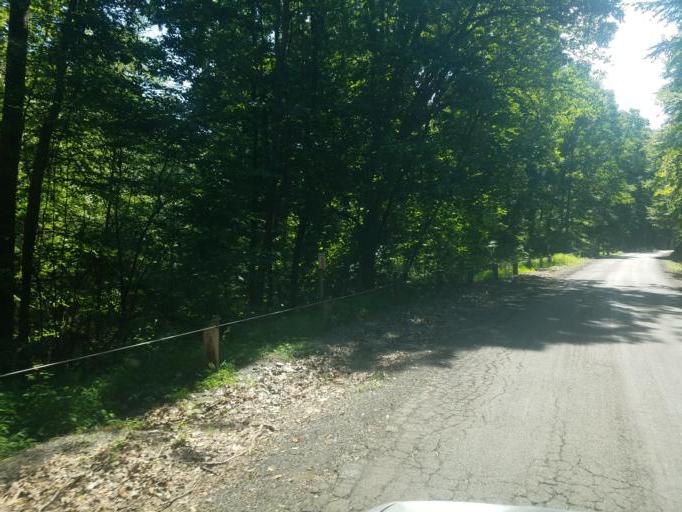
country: US
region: Pennsylvania
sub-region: Clarion County
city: Clarion
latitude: 41.1888
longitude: -79.4348
